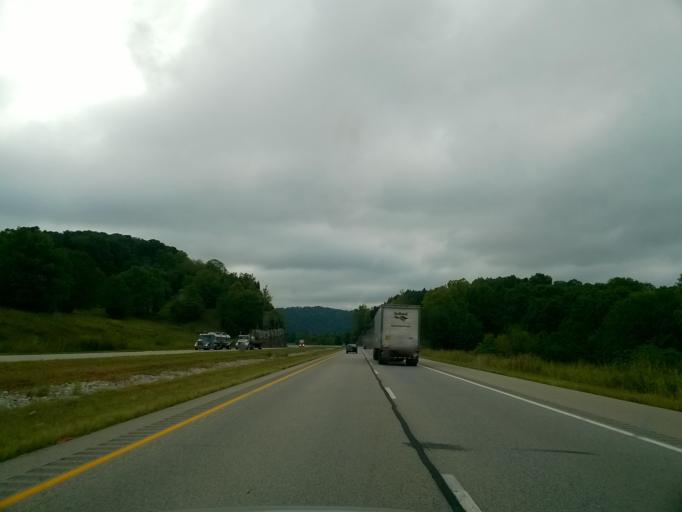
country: US
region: Indiana
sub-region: Harrison County
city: Corydon
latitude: 38.2361
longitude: -86.2408
